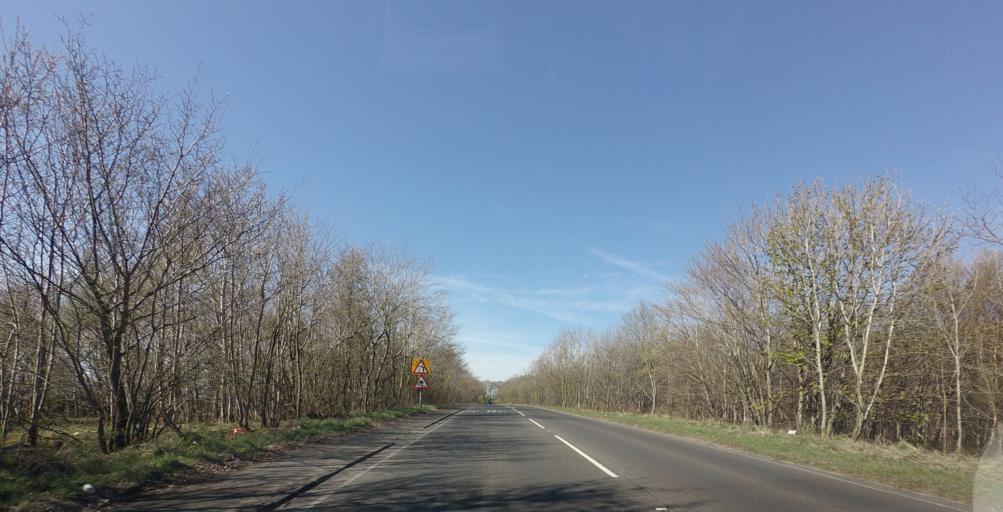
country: GB
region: Scotland
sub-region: West Lothian
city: West Calder
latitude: 55.8840
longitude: -3.5751
